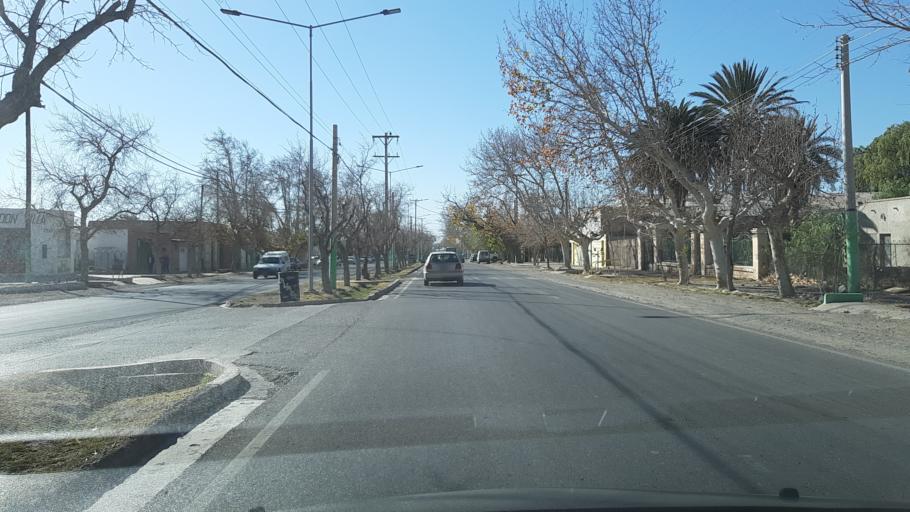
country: AR
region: San Juan
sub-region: Departamento de Rivadavia
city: Rivadavia
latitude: -31.5262
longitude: -68.6312
